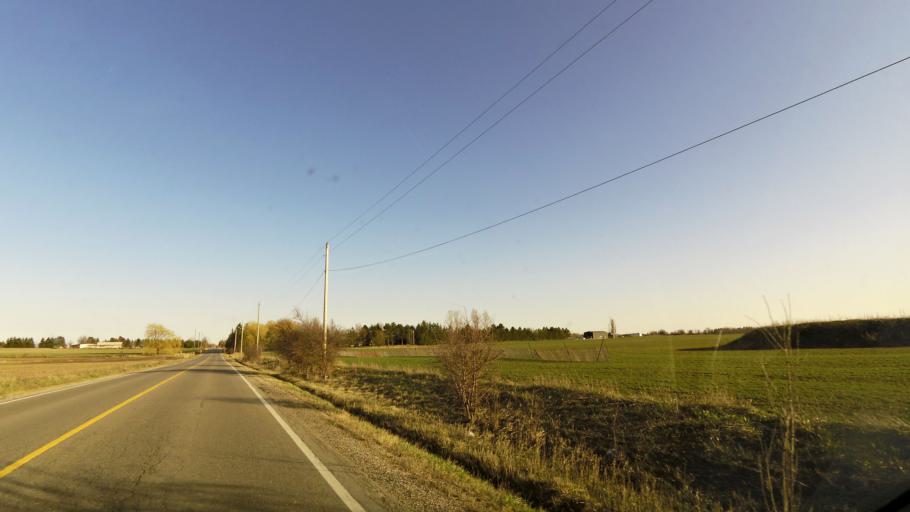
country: CA
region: Ontario
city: Brampton
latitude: 43.8363
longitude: -79.7025
